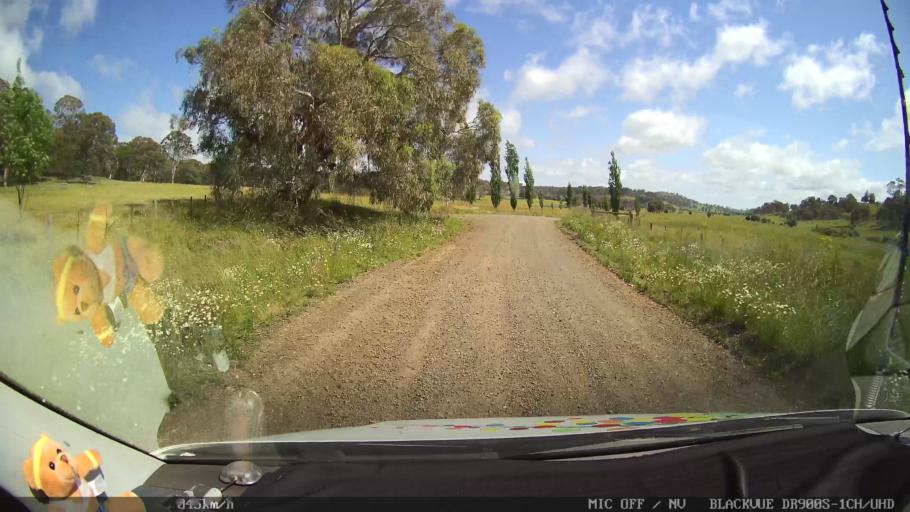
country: AU
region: New South Wales
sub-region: Glen Innes Severn
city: Glen Innes
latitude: -29.9737
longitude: 151.6992
